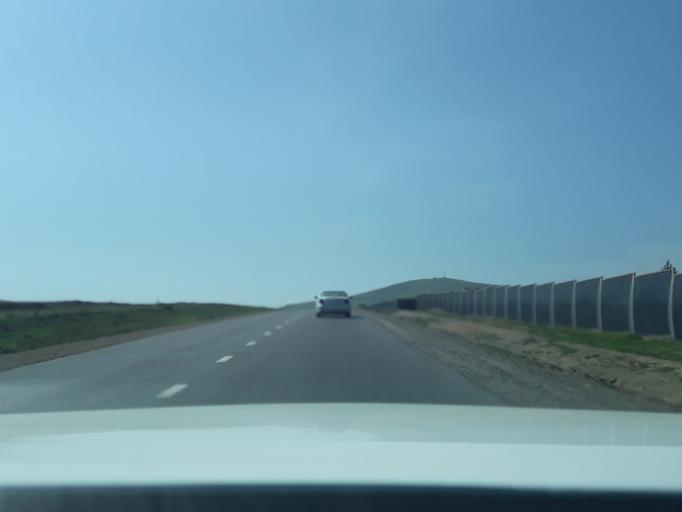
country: MN
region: Ulaanbaatar
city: Ulaanbaatar
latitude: 47.8047
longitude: 106.7490
